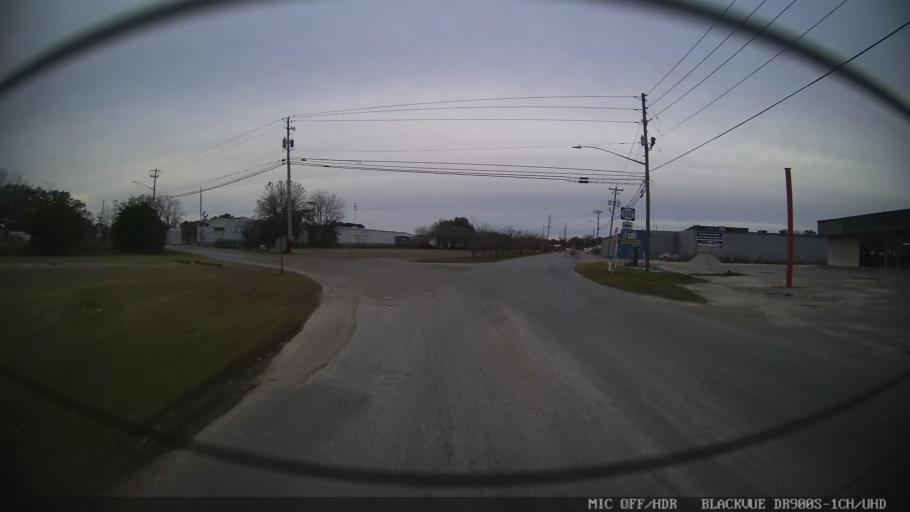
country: US
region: Mississippi
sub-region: Clarke County
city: Quitman
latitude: 32.0388
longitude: -88.7301
